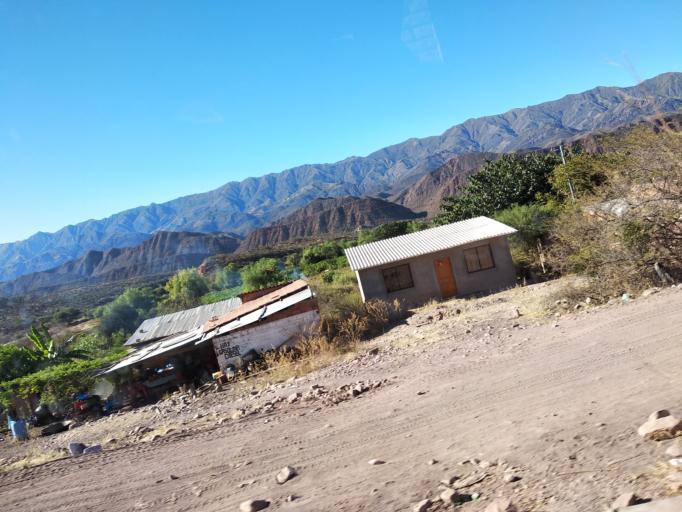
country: BO
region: Cochabamba
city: Mizque
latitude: -18.0785
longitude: -65.7443
